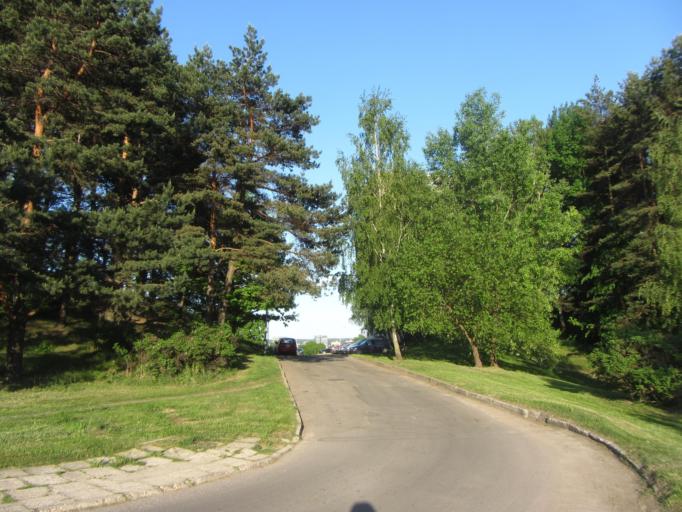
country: LT
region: Vilnius County
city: Seskine
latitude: 54.7266
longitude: 25.2696
